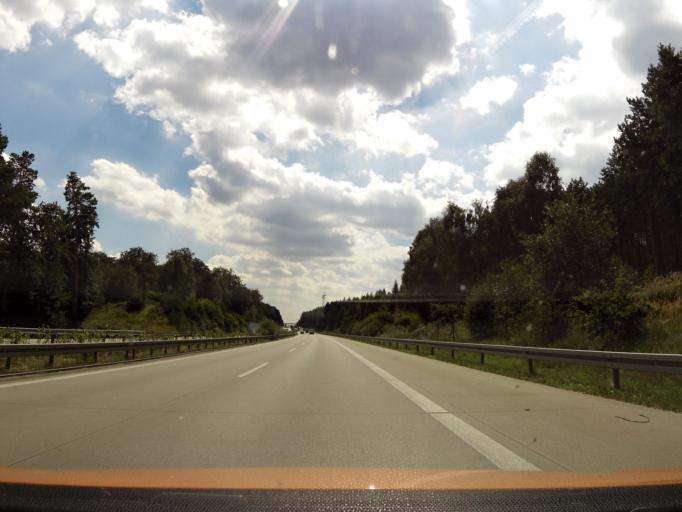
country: DE
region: Brandenburg
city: Wandlitz
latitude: 52.7533
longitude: 13.5429
